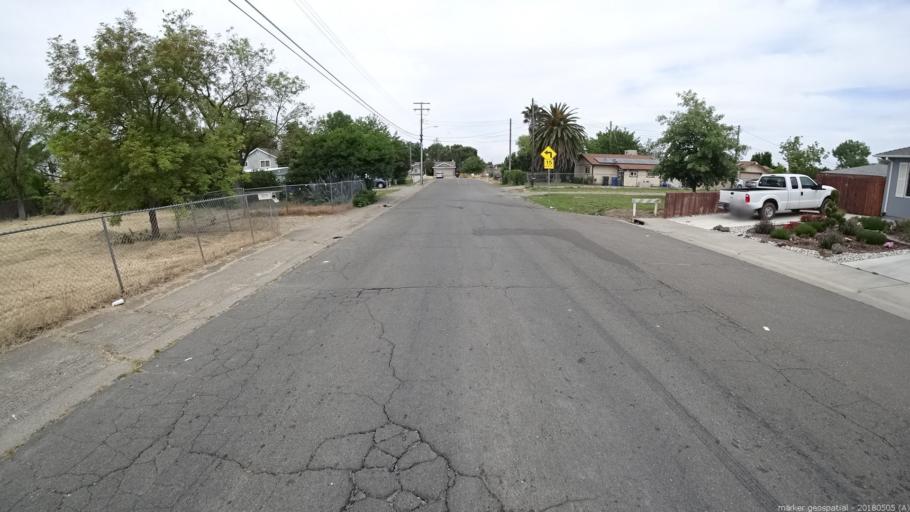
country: US
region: California
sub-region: Sacramento County
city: Rio Linda
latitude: 38.6505
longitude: -121.4616
